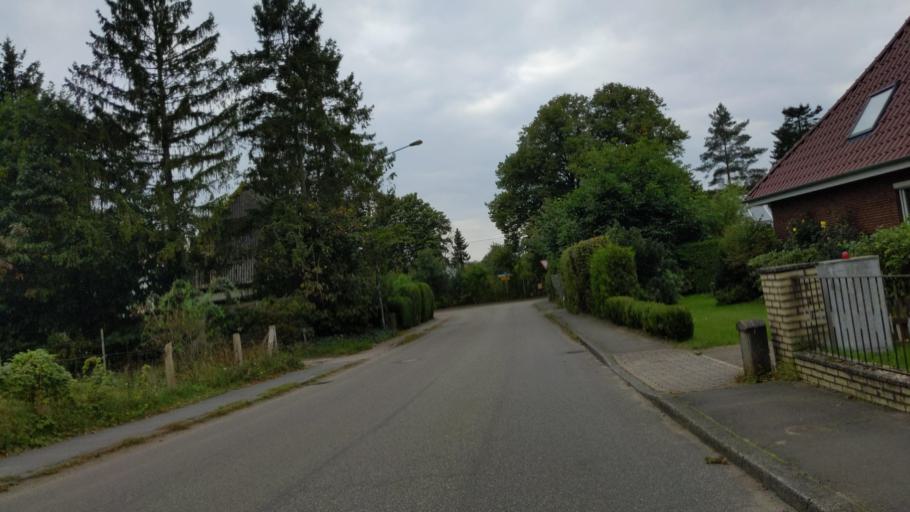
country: DE
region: Schleswig-Holstein
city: Klempau
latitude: 53.7879
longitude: 10.6789
